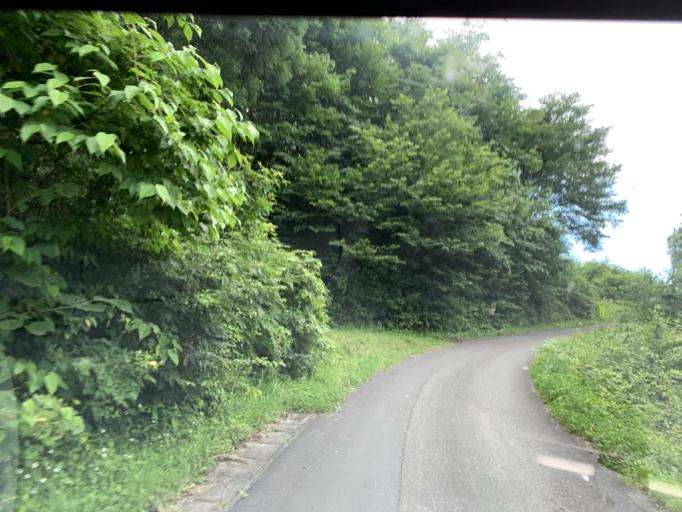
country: JP
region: Iwate
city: Ichinoseki
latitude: 38.9018
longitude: 141.0102
